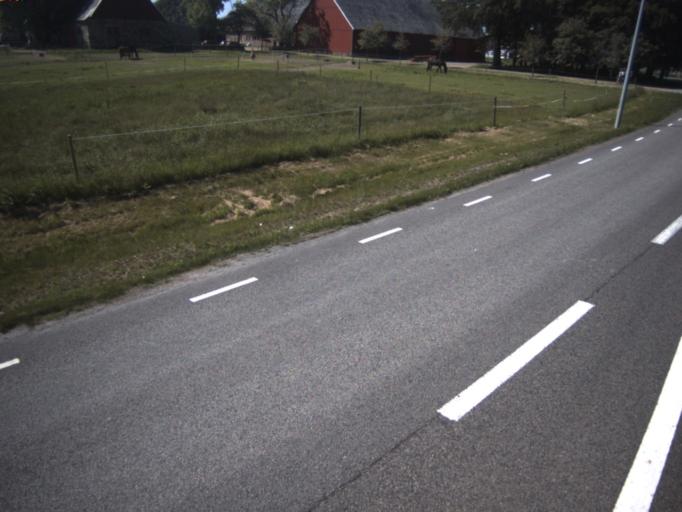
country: SE
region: Skane
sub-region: Helsingborg
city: Barslov
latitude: 56.0411
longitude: 12.7799
